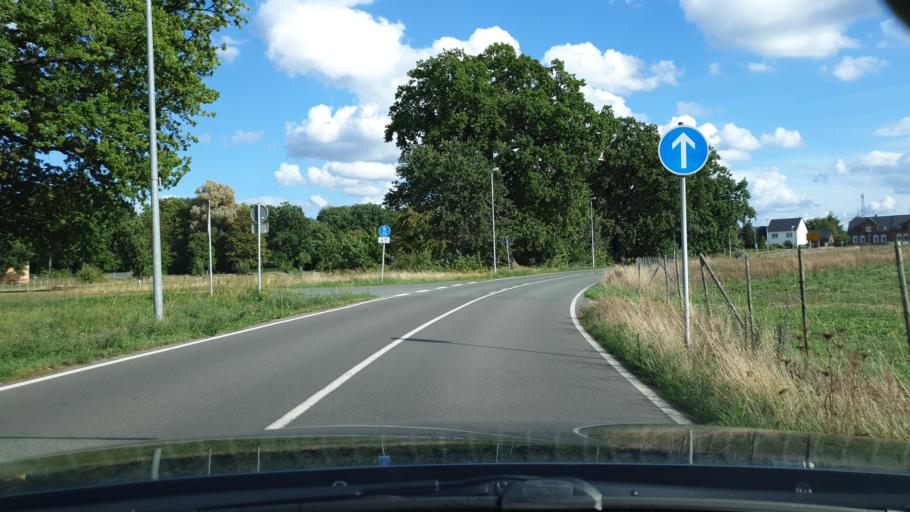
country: DE
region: Saxony-Anhalt
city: Radis
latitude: 51.7518
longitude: 12.5092
